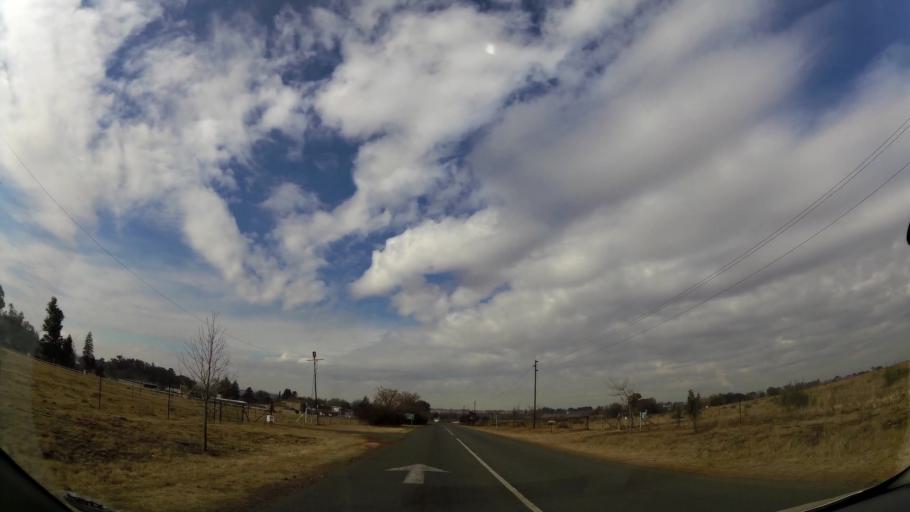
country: ZA
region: Gauteng
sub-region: Sedibeng District Municipality
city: Meyerton
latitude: -26.5550
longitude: 28.0614
